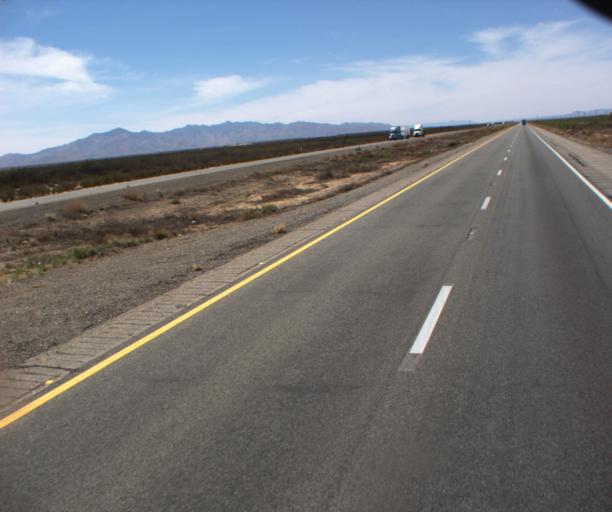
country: US
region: Arizona
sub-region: Cochise County
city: Willcox
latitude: 32.2804
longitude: -109.2794
